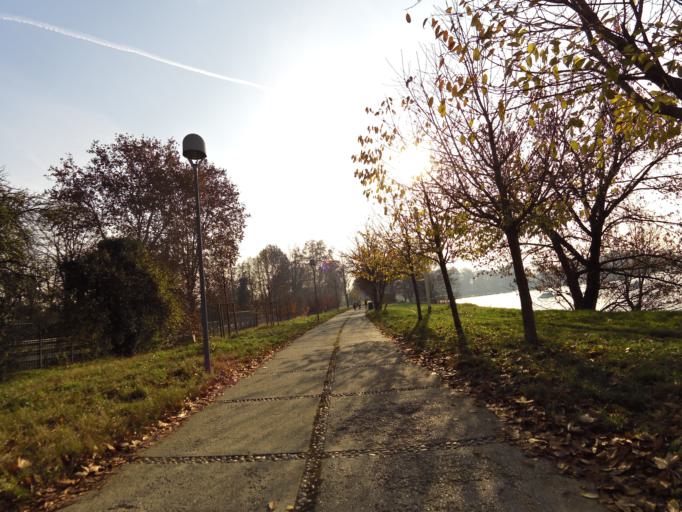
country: IT
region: Lombardy
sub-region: Citta metropolitana di Milano
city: Mezzate
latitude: 45.4554
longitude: 9.2916
